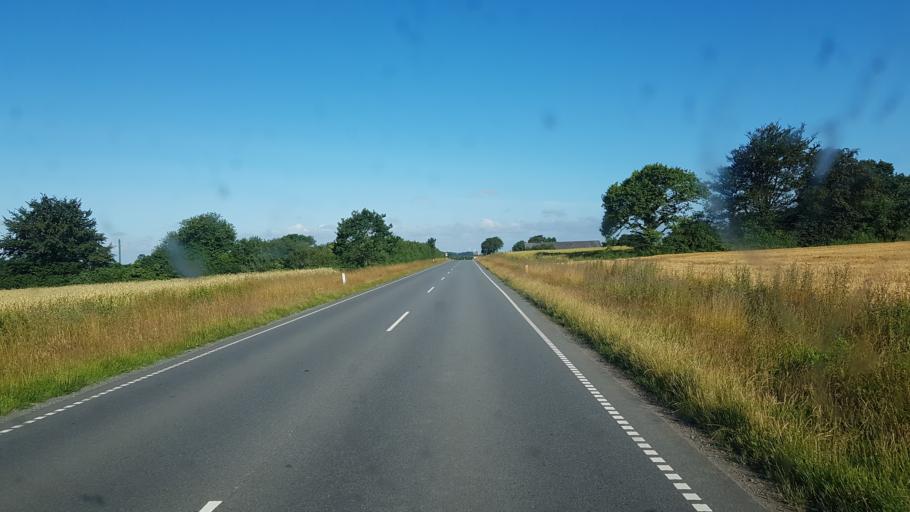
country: DK
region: South Denmark
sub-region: Vejen Kommune
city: Rodding
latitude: 55.3748
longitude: 9.0702
